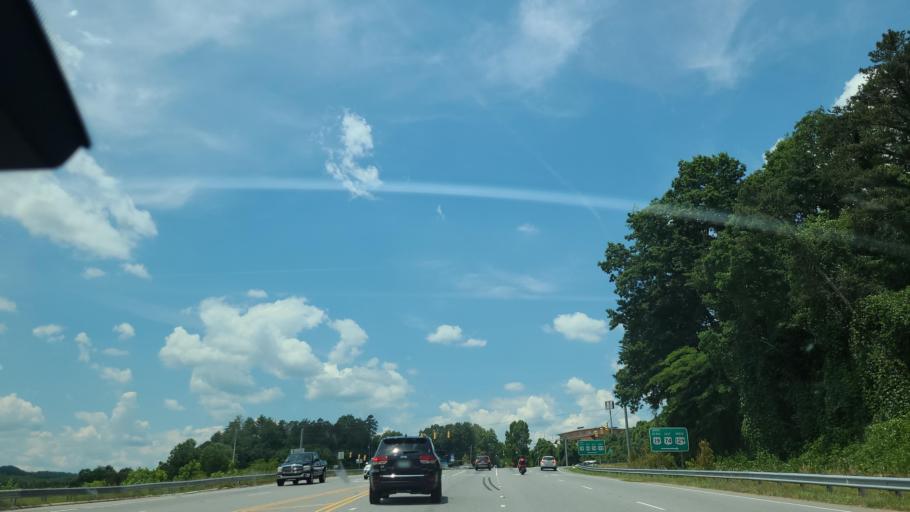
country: US
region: North Carolina
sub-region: Cherokee County
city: Murphy
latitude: 35.0807
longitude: -84.0268
